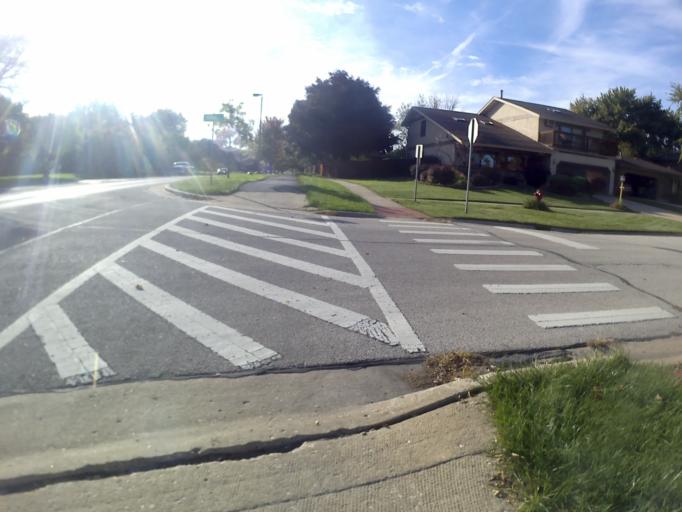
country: US
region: Illinois
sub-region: DuPage County
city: Woodridge
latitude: 41.7359
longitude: -88.0447
